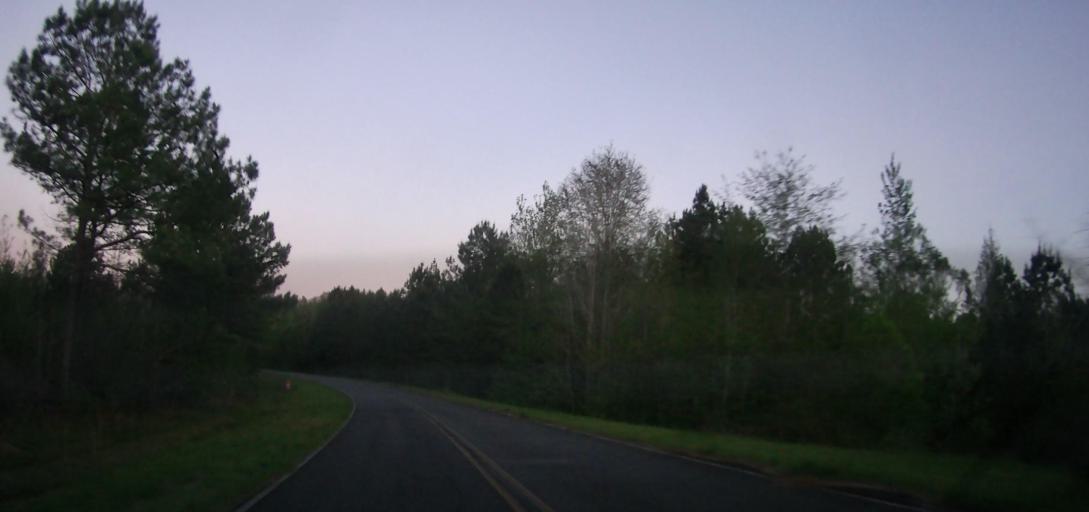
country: US
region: Georgia
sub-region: Marion County
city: Buena Vista
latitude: 32.2543
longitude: -84.6418
